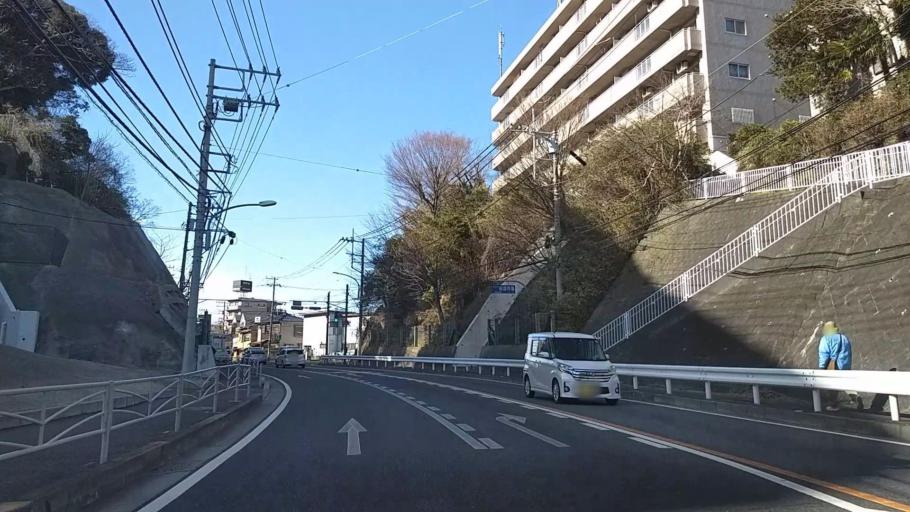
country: JP
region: Kanagawa
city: Yokohama
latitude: 35.3709
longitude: 139.6336
